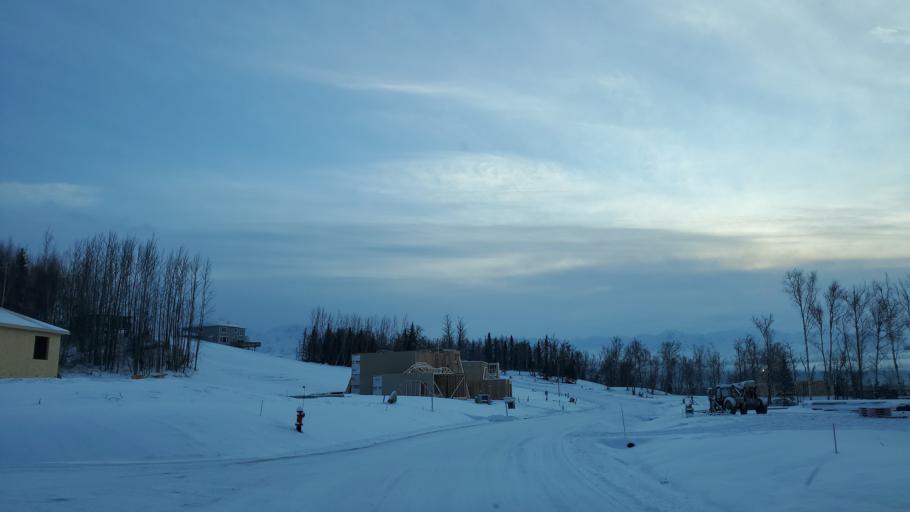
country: US
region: Alaska
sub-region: Matanuska-Susitna Borough
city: Lakes
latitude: 61.5477
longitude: -149.3271
